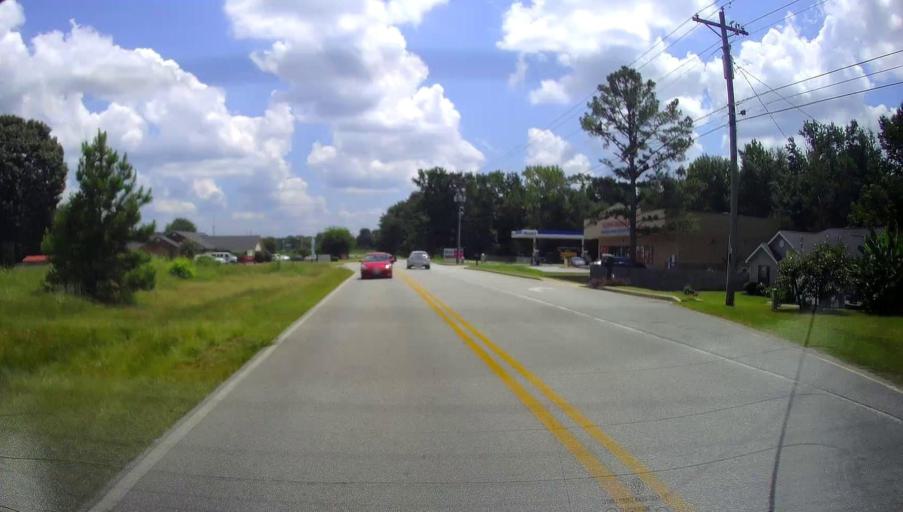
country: US
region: Georgia
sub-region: Houston County
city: Centerville
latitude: 32.6087
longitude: -83.6824
